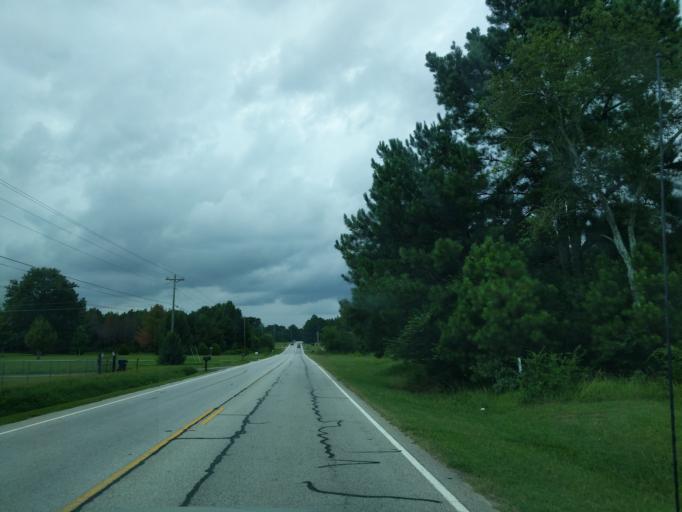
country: US
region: Georgia
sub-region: Walton County
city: Loganville
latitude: 33.7955
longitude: -83.9552
